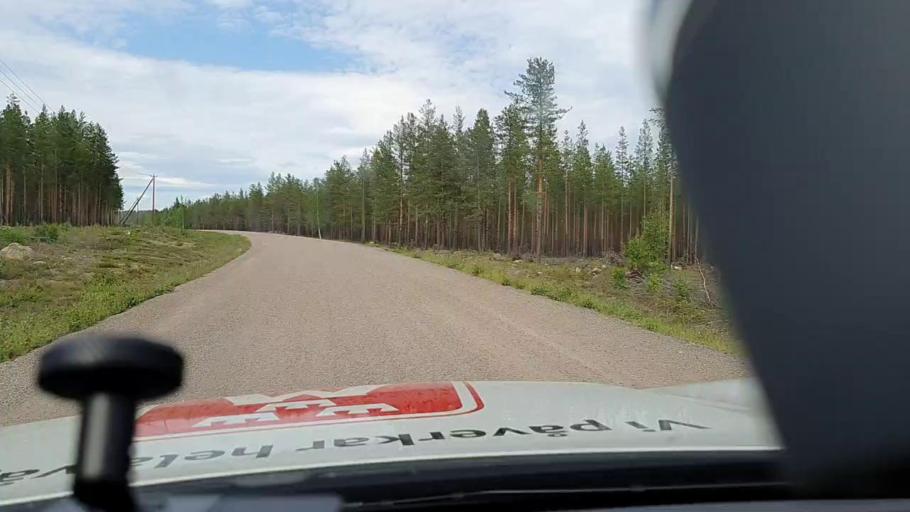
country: SE
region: Norrbotten
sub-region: Alvsbyns Kommun
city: AElvsbyn
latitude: 66.1218
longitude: 20.9913
